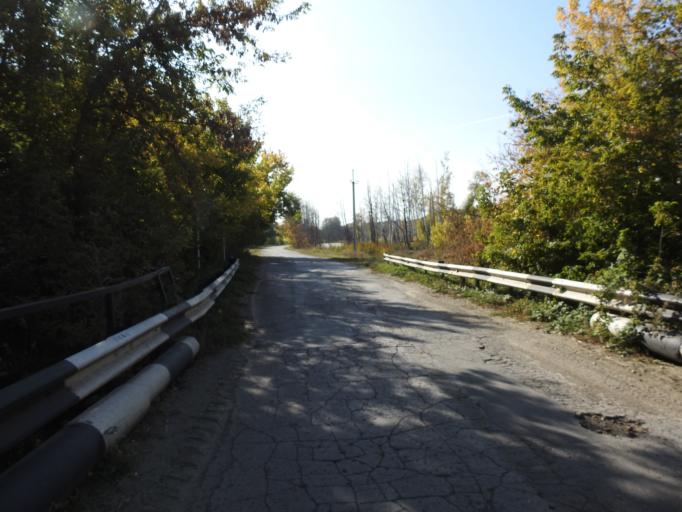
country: RU
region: Saratov
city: Baltay
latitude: 52.4715
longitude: 46.6759
